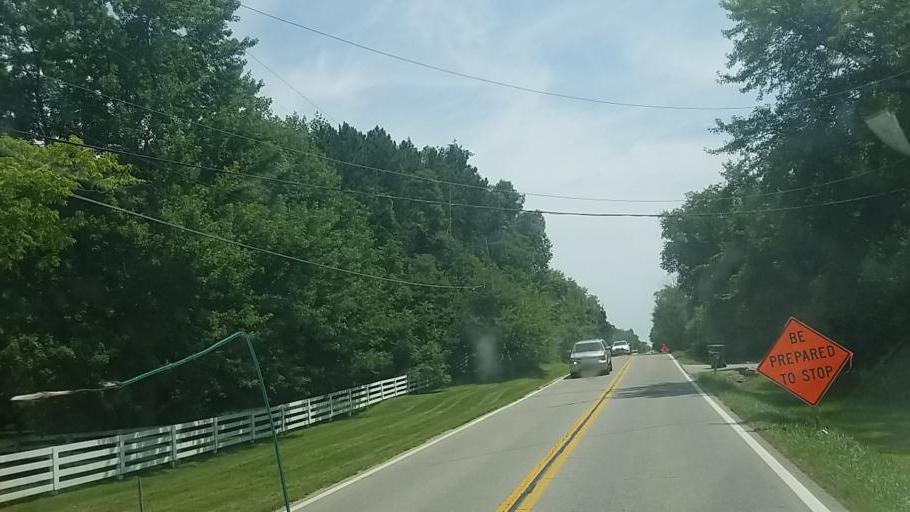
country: US
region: Ohio
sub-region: Franklin County
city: New Albany
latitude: 40.0528
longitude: -82.8071
